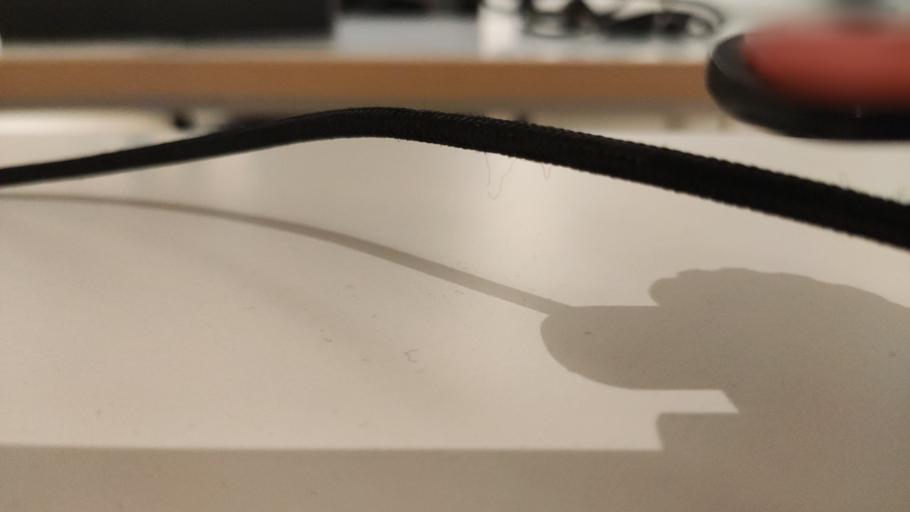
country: RU
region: Moskovskaya
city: Dorokhovo
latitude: 55.4213
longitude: 36.3613
